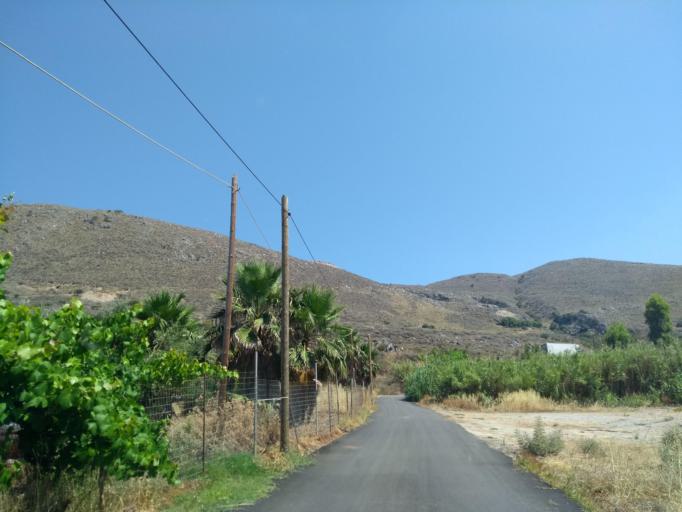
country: GR
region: Crete
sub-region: Nomos Rethymnis
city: Atsipopoulon
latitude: 35.3570
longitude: 24.3684
